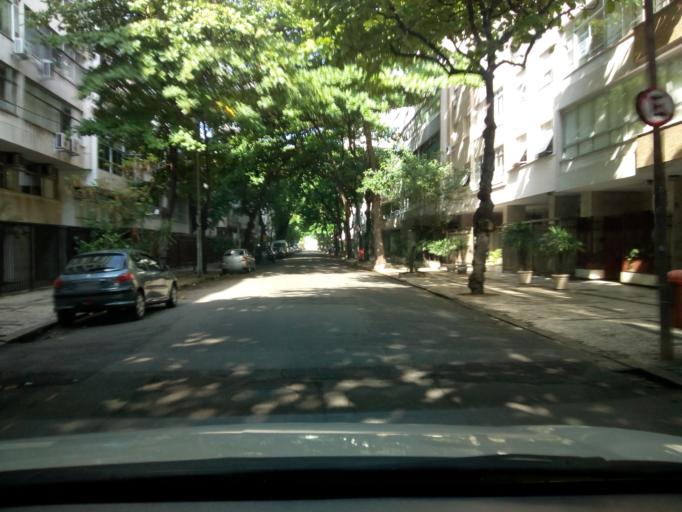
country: BR
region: Rio de Janeiro
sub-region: Rio De Janeiro
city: Rio de Janeiro
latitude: -22.9863
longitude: -43.1926
